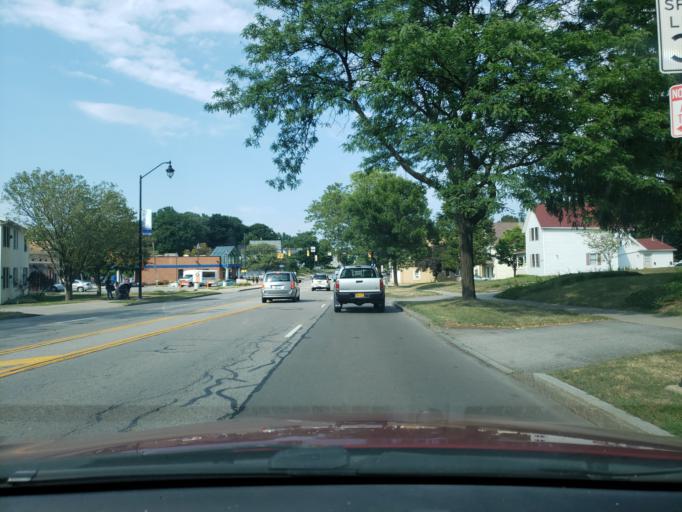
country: US
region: New York
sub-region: Monroe County
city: Irondequoit
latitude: 43.2407
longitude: -77.6209
